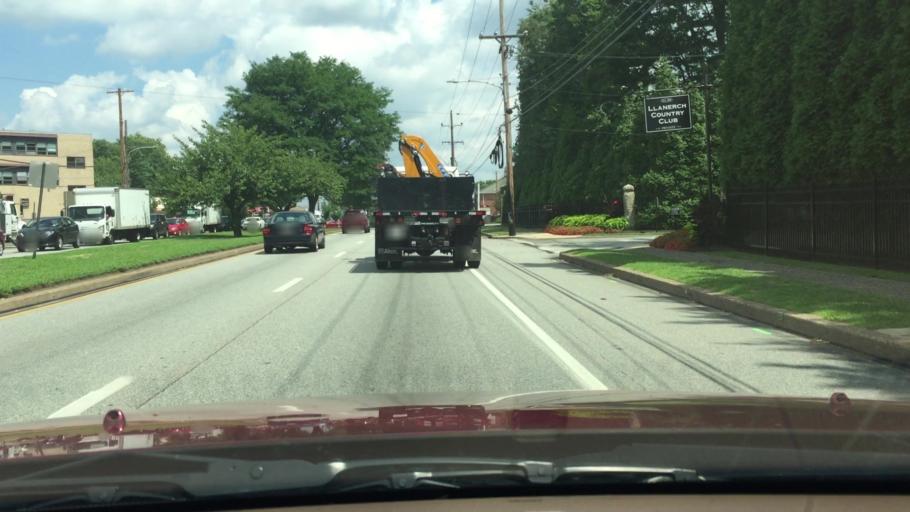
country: US
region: Pennsylvania
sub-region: Delaware County
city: Drexel Hill
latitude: 39.9718
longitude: -75.3131
